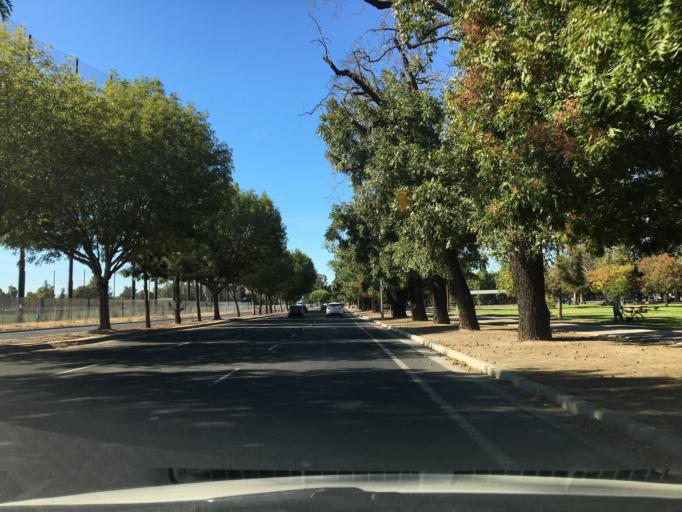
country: US
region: California
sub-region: Santa Clara County
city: San Jose
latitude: 37.3223
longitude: -121.8623
